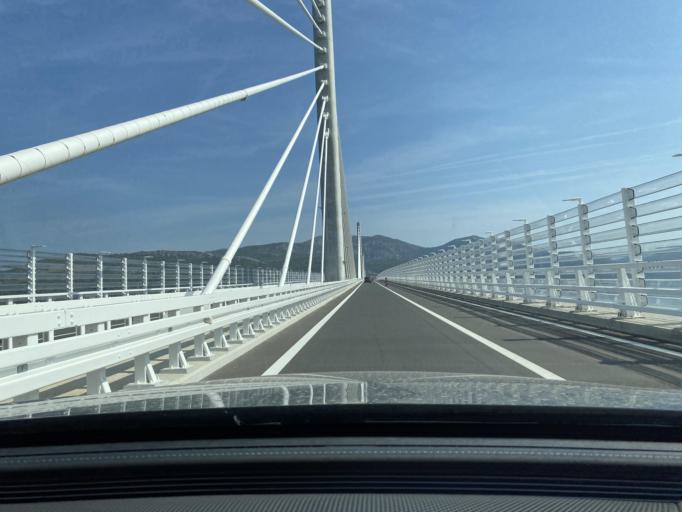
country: BA
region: Federation of Bosnia and Herzegovina
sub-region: Hercegovacko-Bosanski Kanton
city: Neum
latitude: 42.9280
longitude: 17.5324
